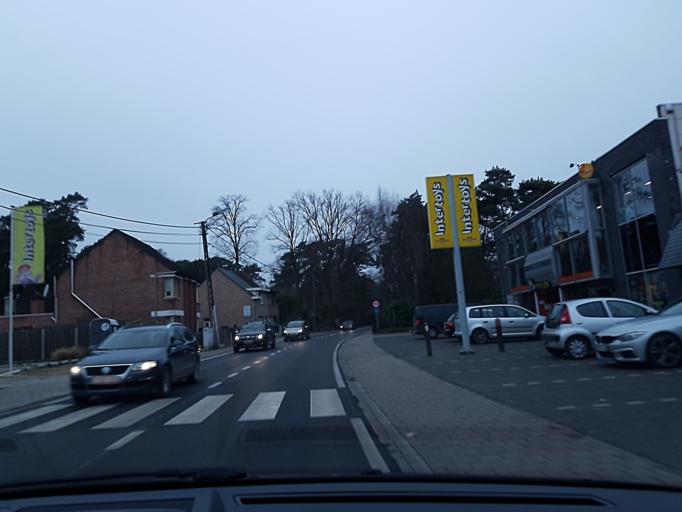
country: BE
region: Flanders
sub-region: Provincie Vlaams-Brabant
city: Keerbergen
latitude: 51.0067
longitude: 4.6181
